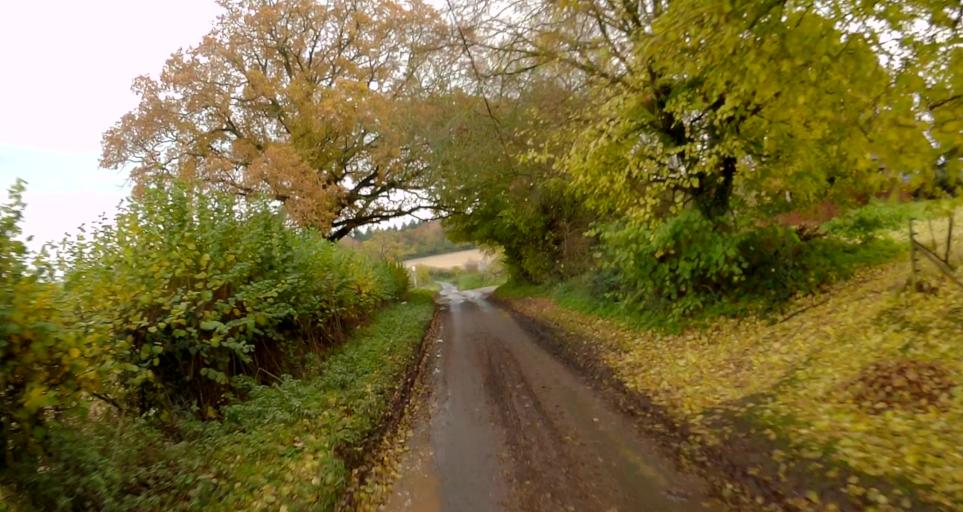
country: GB
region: England
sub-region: Hampshire
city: Long Sutton
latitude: 51.2101
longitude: -0.9557
